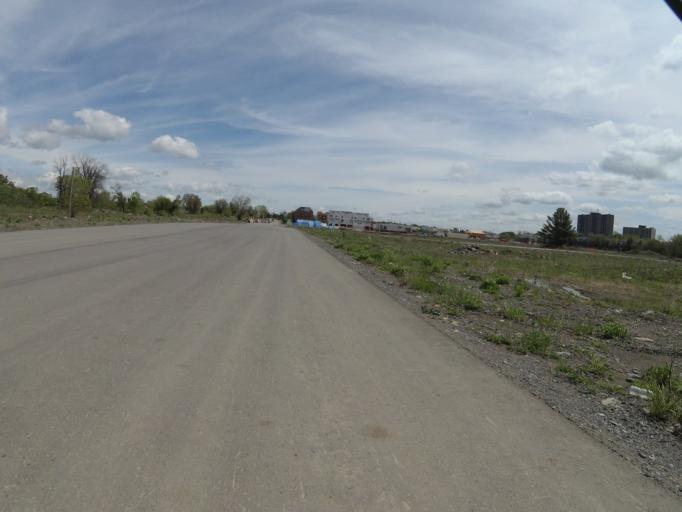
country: CA
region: Quebec
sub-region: Outaouais
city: Gatineau
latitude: 45.4530
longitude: -75.6344
